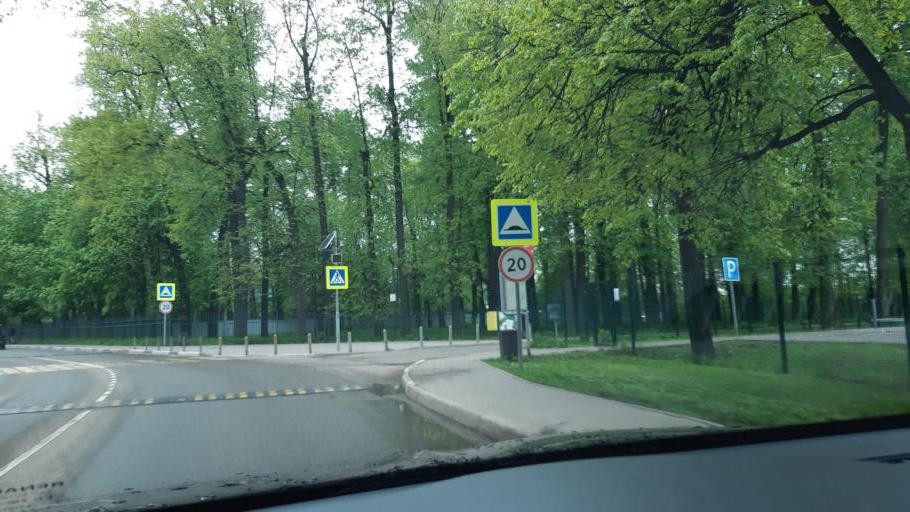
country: RU
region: Moskovskaya
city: Dolgoprudnyy
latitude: 55.9532
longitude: 37.4934
